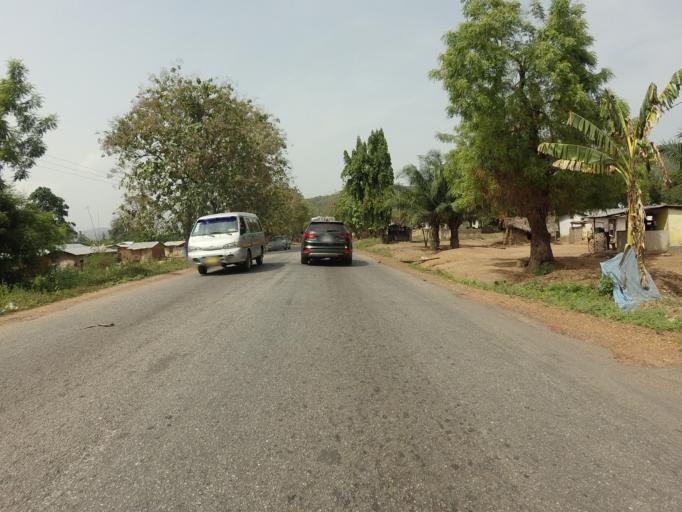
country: GH
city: Akropong
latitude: 6.2409
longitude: 0.1096
